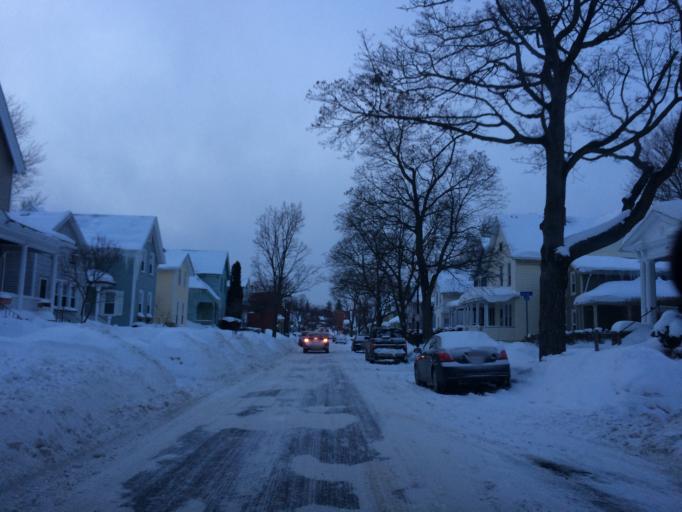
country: US
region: New York
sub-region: Monroe County
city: Rochester
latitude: 43.1392
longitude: -77.6004
